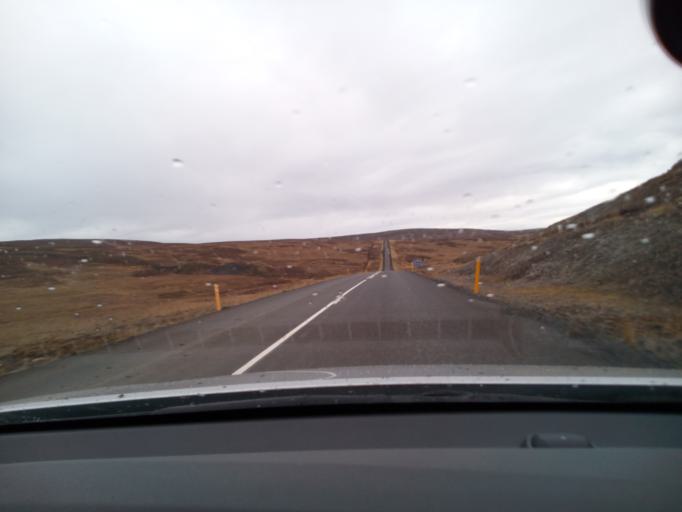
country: IS
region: Northeast
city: Laugar
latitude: 65.7946
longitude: -17.2386
